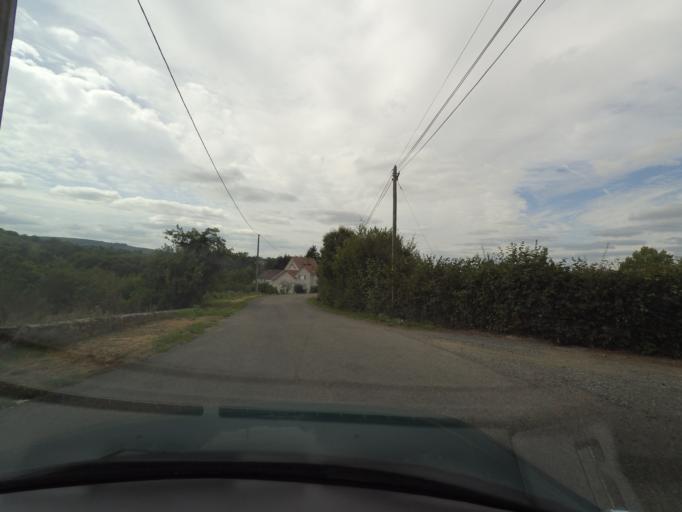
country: FR
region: Limousin
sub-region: Departement de la Haute-Vienne
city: Bussiere-Galant
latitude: 45.6733
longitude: 1.0783
